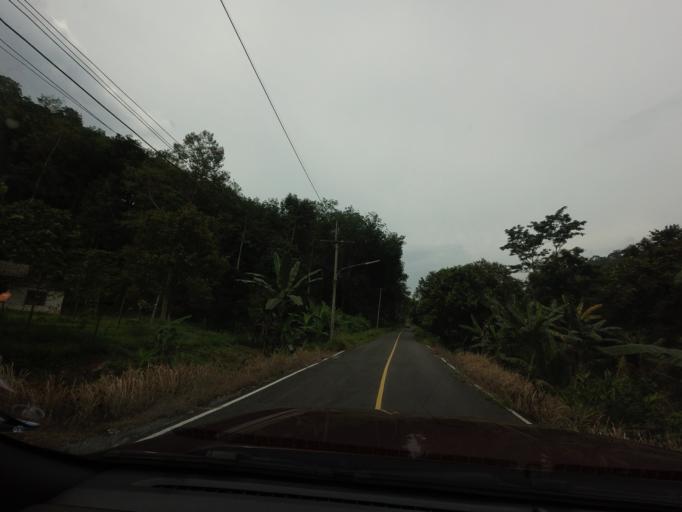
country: TH
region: Narathiwat
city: Si Sakhon
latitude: 6.0621
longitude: 101.3888
